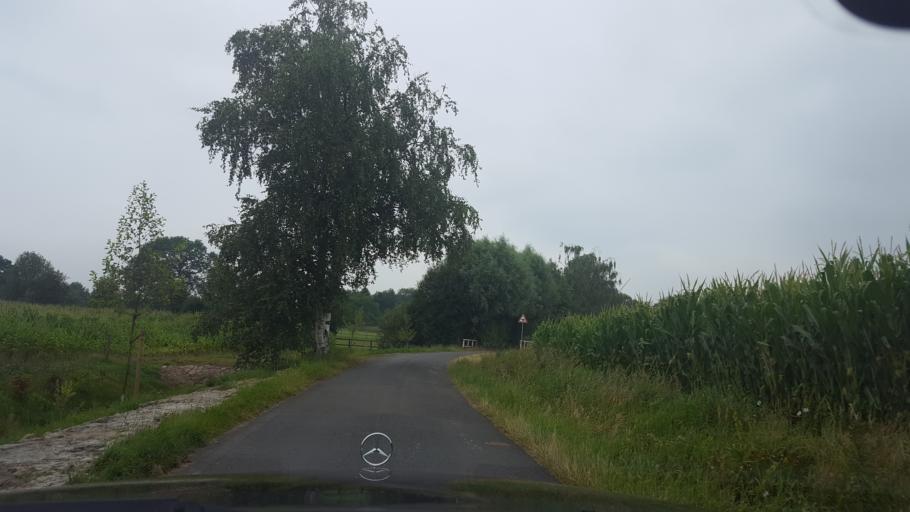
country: DE
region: North Rhine-Westphalia
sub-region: Regierungsbezirk Munster
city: Recklinghausen
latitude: 51.6593
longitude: 7.2039
